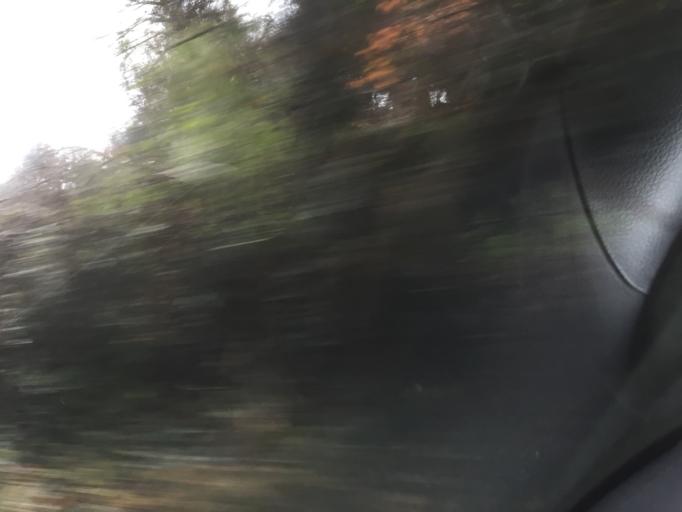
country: GB
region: England
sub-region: South Gloucestershire
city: Hinton
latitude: 51.5031
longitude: -2.3603
